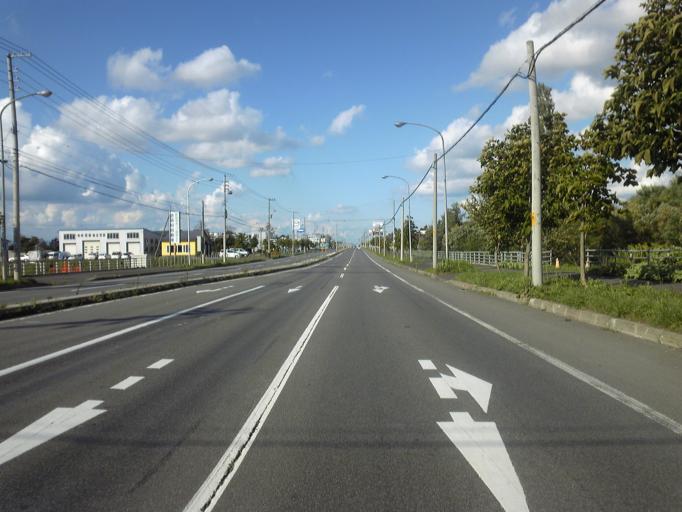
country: JP
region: Hokkaido
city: Bibai
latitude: 43.3421
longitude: 141.8634
